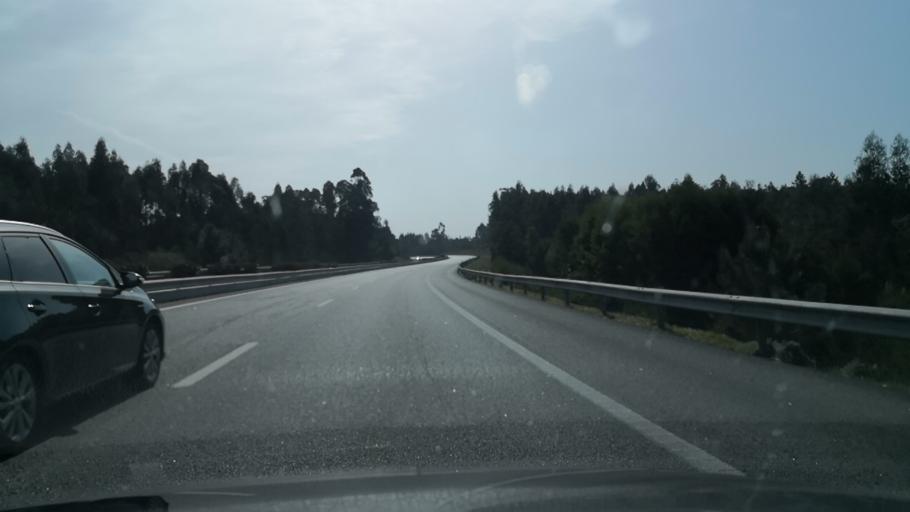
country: PT
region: Aveiro
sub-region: Albergaria-A-Velha
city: Albergaria-a-Velha
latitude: 40.6593
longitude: -8.5154
